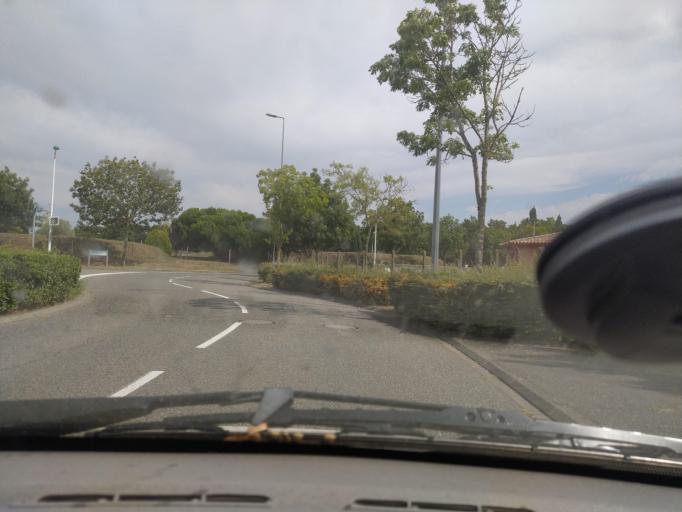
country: FR
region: Midi-Pyrenees
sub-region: Departement de la Haute-Garonne
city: Tournefeuille
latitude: 43.5930
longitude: 1.3148
